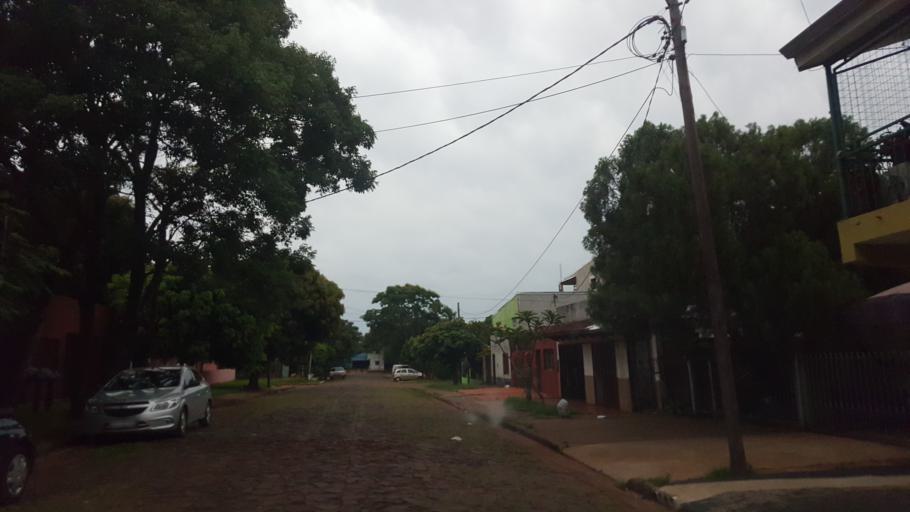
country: AR
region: Misiones
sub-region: Departamento de Capital
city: Posadas
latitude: -27.3659
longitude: -55.9297
